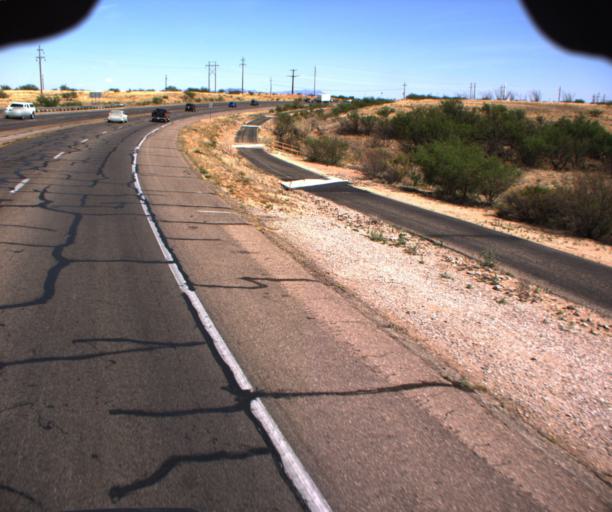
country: US
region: Arizona
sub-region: Cochise County
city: Sierra Vista
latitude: 31.5741
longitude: -110.3135
